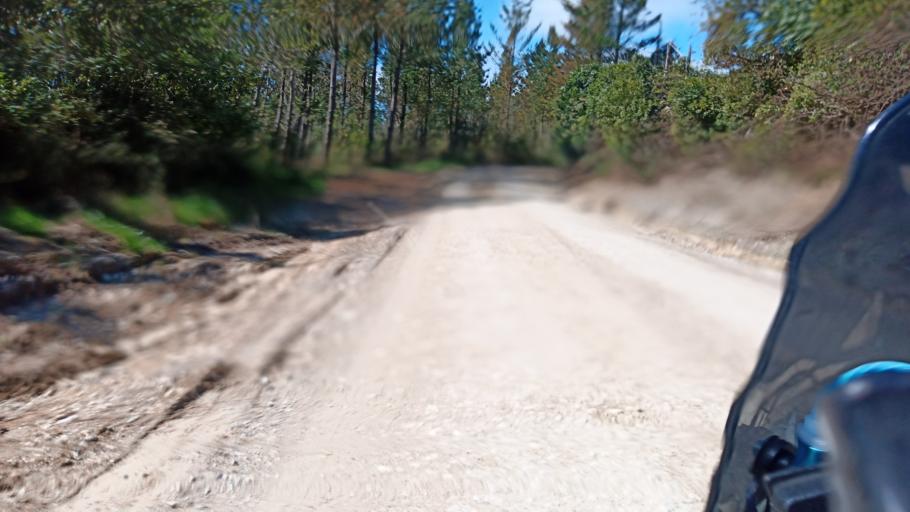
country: NZ
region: Gisborne
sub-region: Gisborne District
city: Gisborne
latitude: -38.9076
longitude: 177.8117
